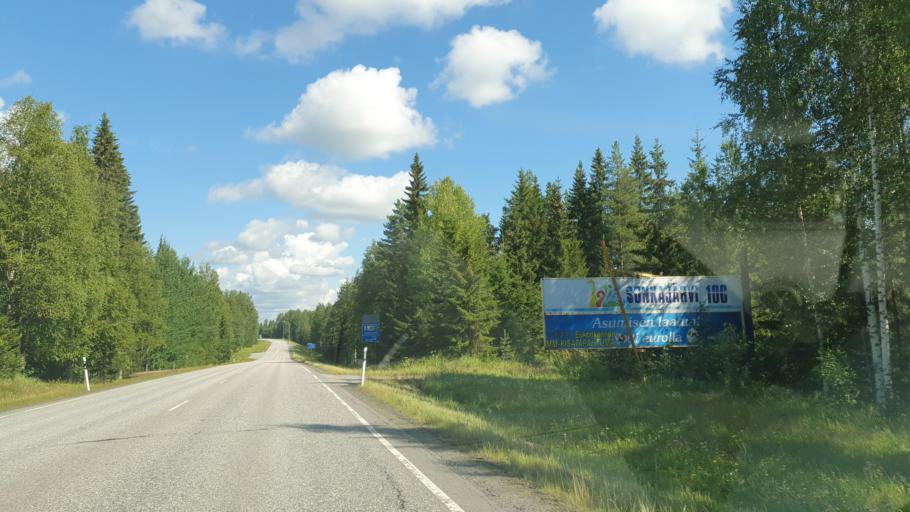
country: FI
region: Northern Savo
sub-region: Ylae-Savo
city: Sonkajaervi
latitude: 63.6921
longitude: 27.3495
